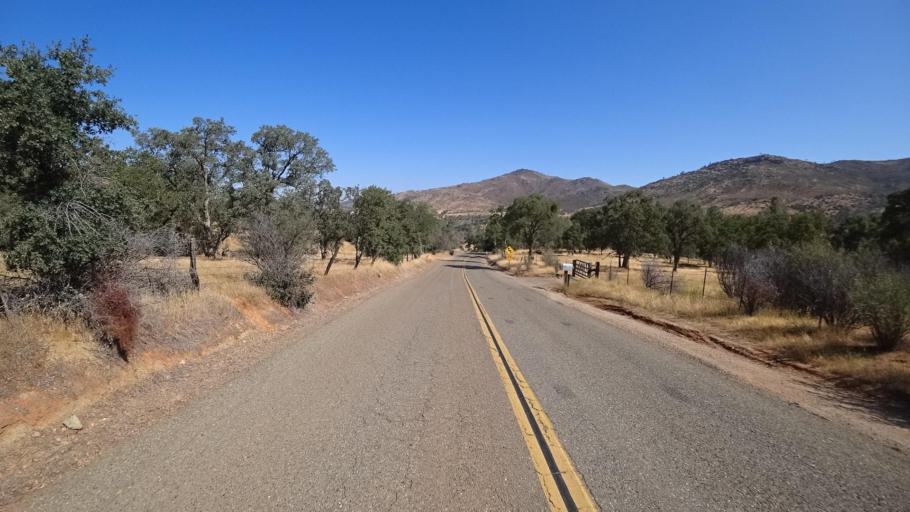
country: US
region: California
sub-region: Mariposa County
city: Mariposa
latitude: 37.5710
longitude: -120.1690
